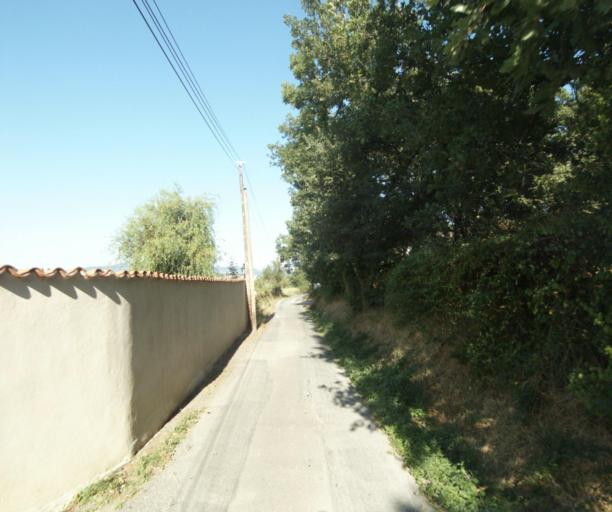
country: FR
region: Rhone-Alpes
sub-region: Departement du Rhone
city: Lentilly
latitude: 45.8011
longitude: 4.6810
